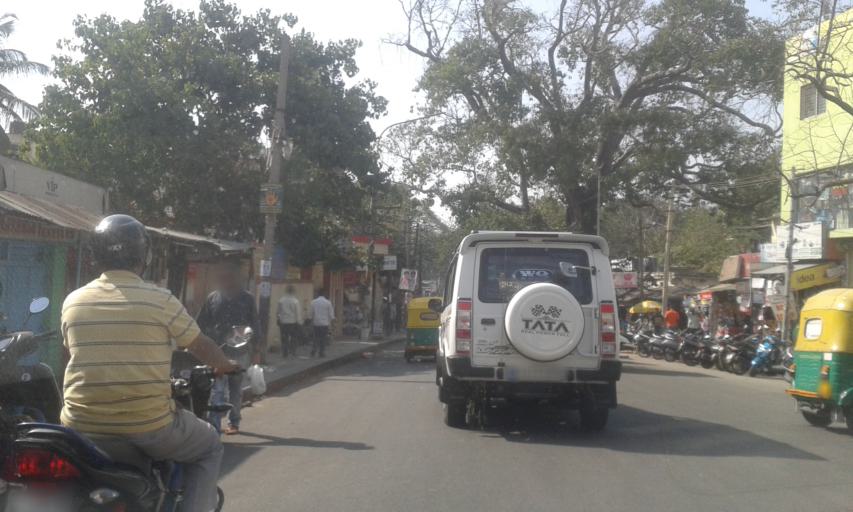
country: IN
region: Karnataka
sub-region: Bangalore Urban
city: Bangalore
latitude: 13.0191
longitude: 77.5572
